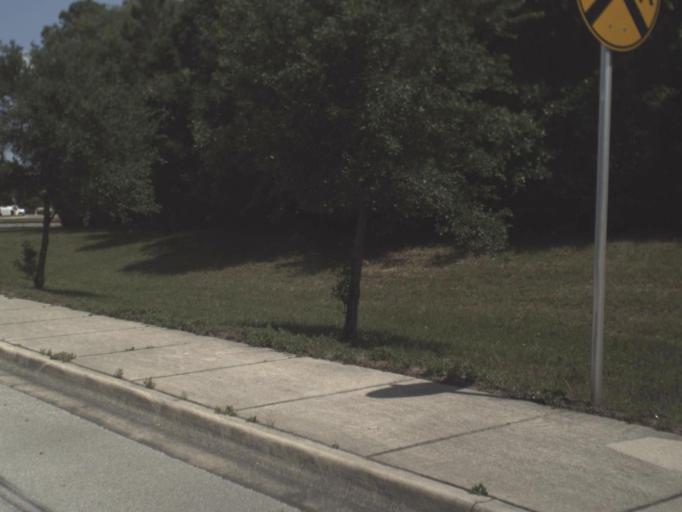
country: US
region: Florida
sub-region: Duval County
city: Jacksonville
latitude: 30.4120
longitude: -81.5684
